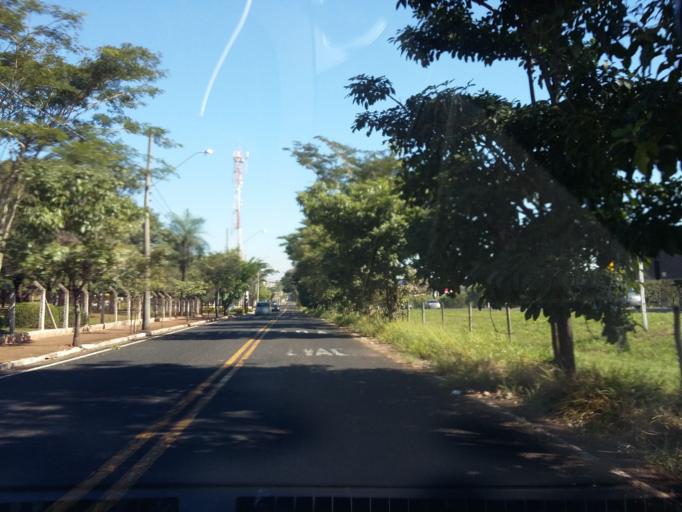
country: BR
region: Sao Paulo
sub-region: Sao Jose Do Rio Preto
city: Sao Jose do Rio Preto
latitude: -20.8326
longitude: -49.3629
